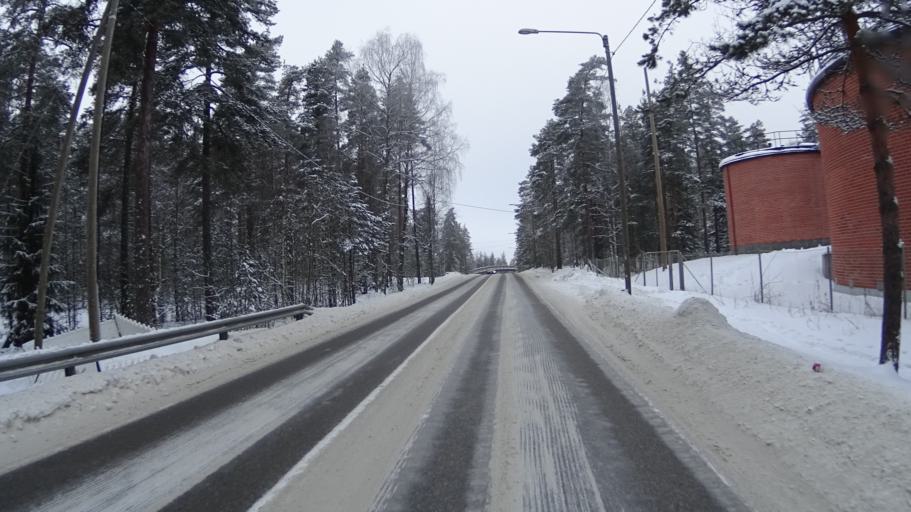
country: FI
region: Uusimaa
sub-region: Helsinki
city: Vihti
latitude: 60.3389
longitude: 24.3096
